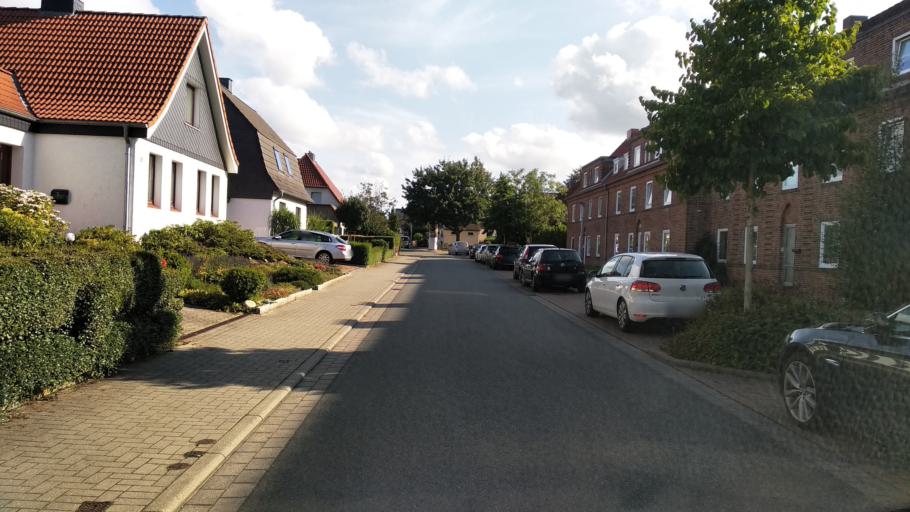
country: DE
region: Schleswig-Holstein
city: Schleswig
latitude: 54.5209
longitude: 9.5529
